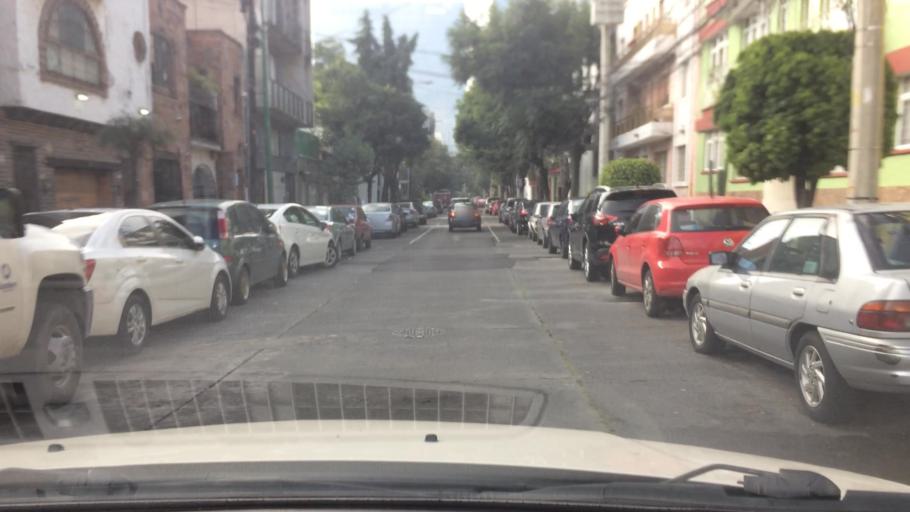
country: MX
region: Mexico City
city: Alvaro Obregon
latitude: 19.3664
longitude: -99.1898
